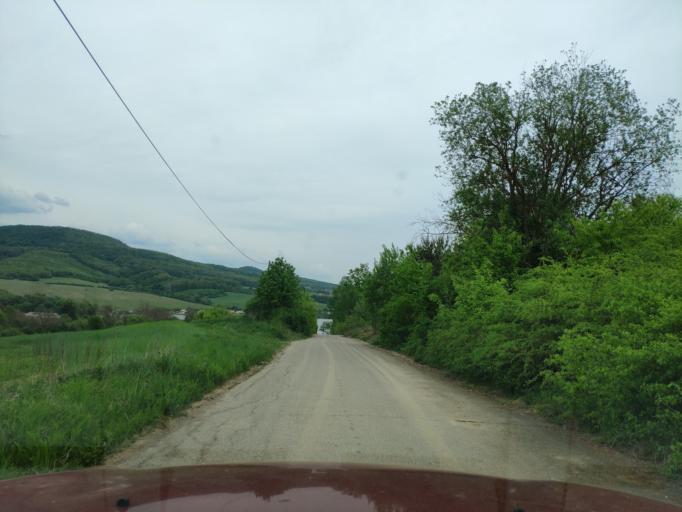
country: SK
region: Banskobystricky
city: Rimavska Sobota
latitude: 48.4846
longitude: 20.0846
